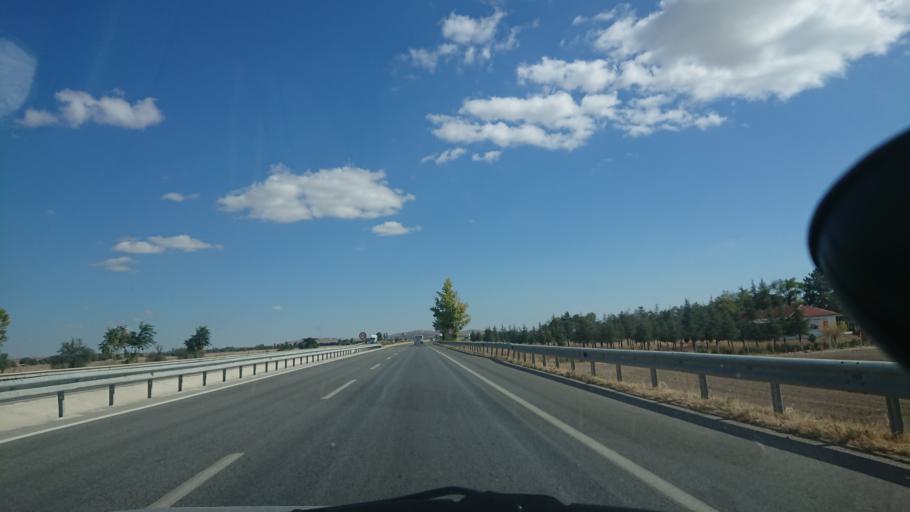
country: TR
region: Eskisehir
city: Mahmudiye
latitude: 39.5410
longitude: 30.9387
